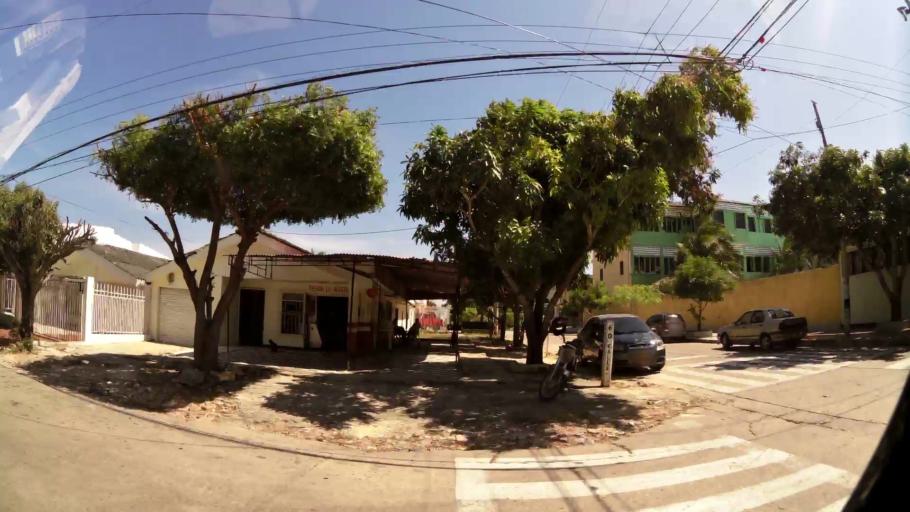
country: CO
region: Atlantico
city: Barranquilla
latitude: 10.9809
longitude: -74.7996
